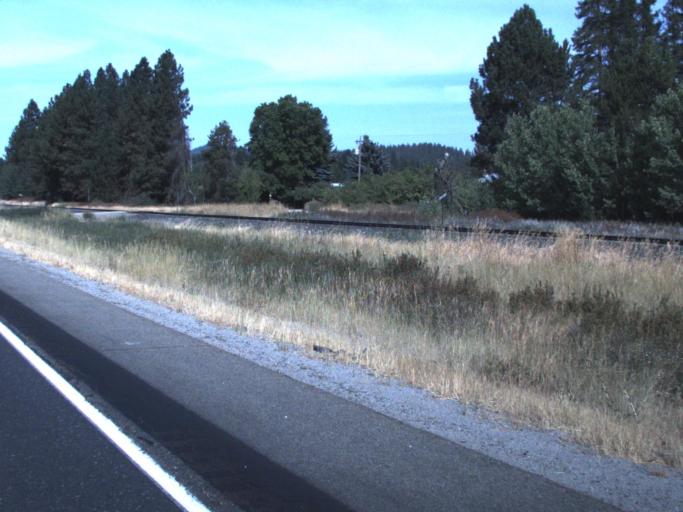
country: US
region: Washington
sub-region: Spokane County
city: Deer Park
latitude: 47.9915
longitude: -117.5429
